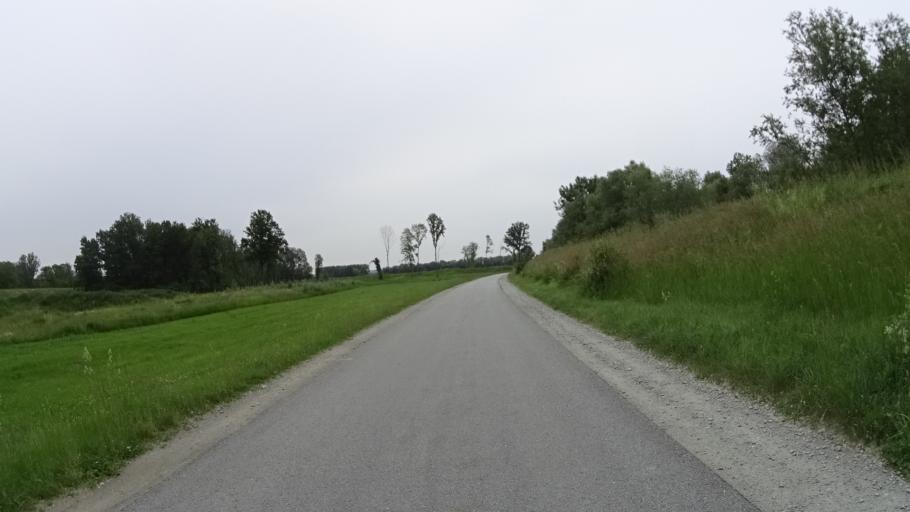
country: DE
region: Bavaria
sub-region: Lower Bavaria
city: Niederalteich
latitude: 48.7889
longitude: 13.0052
